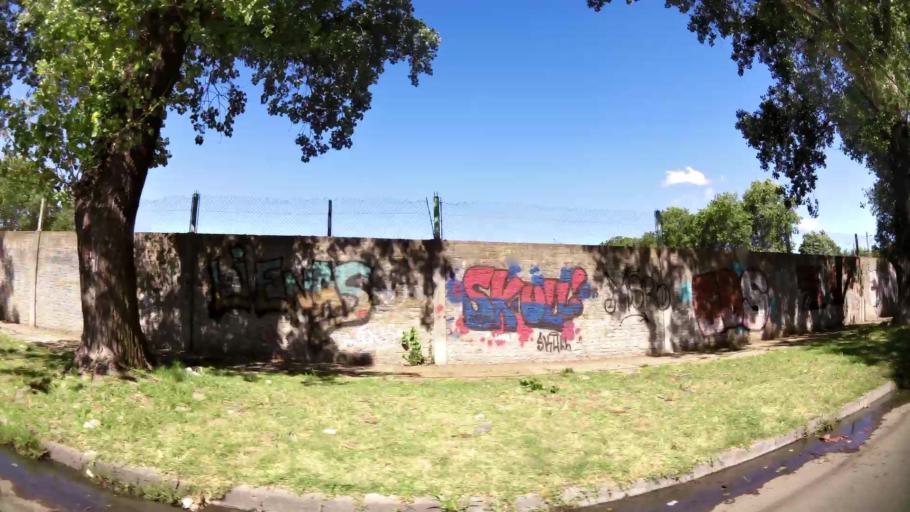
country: AR
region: Buenos Aires
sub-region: Partido de Lomas de Zamora
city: Lomas de Zamora
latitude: -34.7491
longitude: -58.4179
